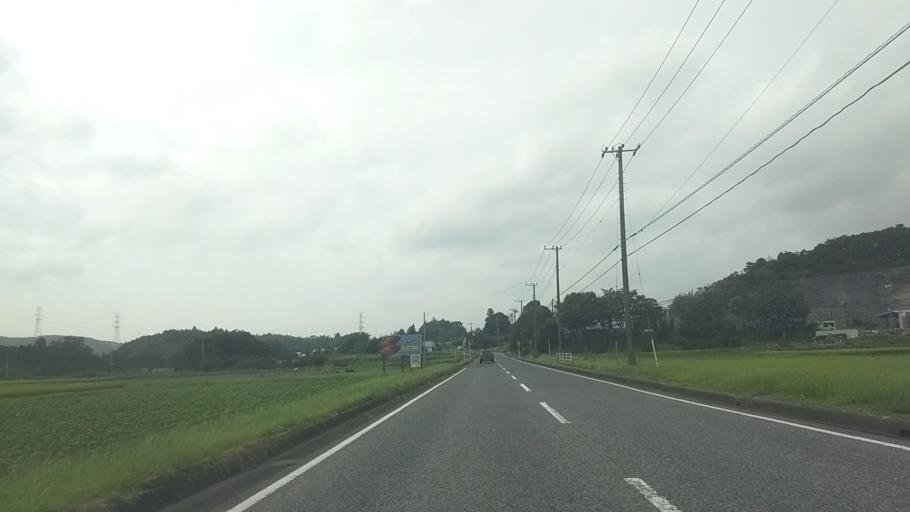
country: JP
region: Chiba
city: Kimitsu
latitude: 35.2746
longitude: 139.9949
